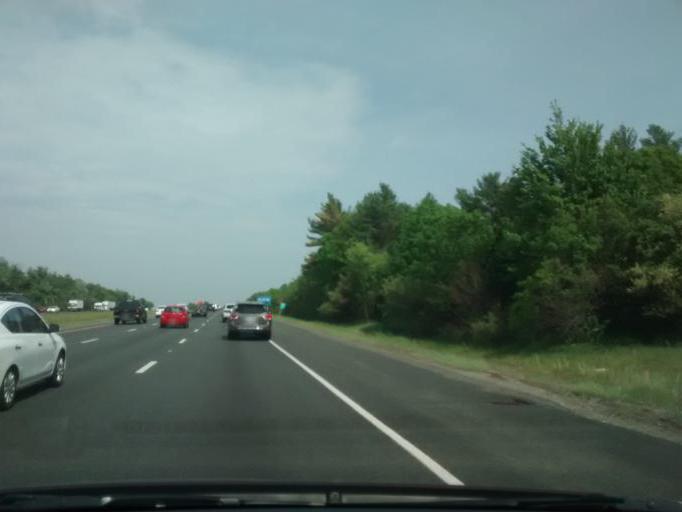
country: US
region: Massachusetts
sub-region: Bristol County
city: Raynham
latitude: 41.9595
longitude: -71.0805
